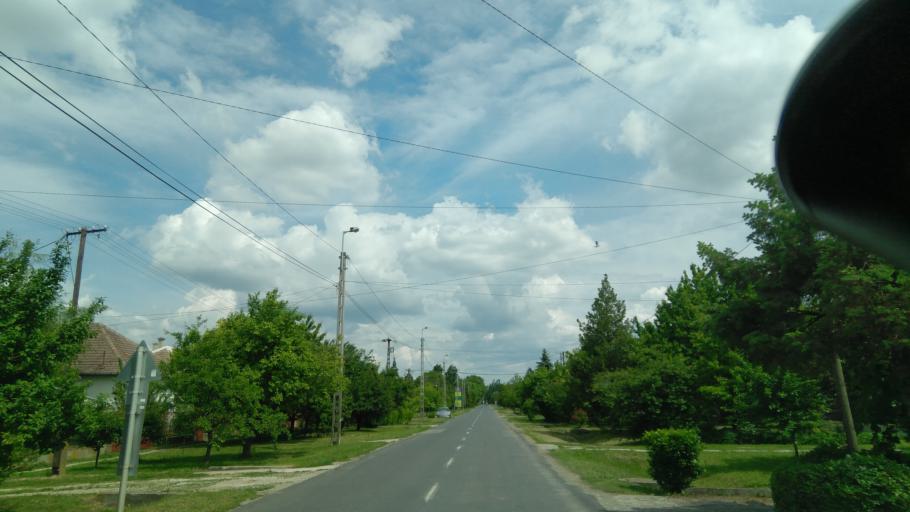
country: HU
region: Bekes
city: Totkomlos
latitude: 46.4122
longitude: 20.7270
